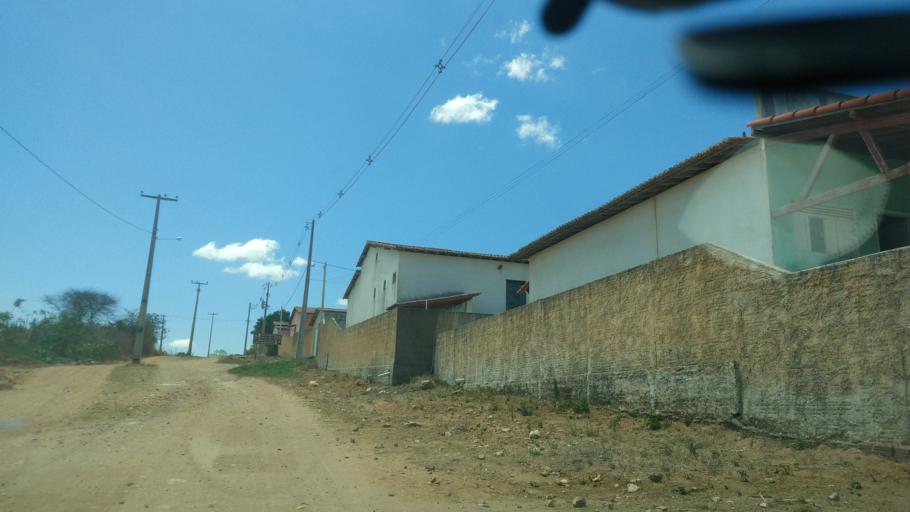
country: BR
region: Rio Grande do Norte
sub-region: Cerro Cora
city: Cerro Cora
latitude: -6.0335
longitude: -36.3443
